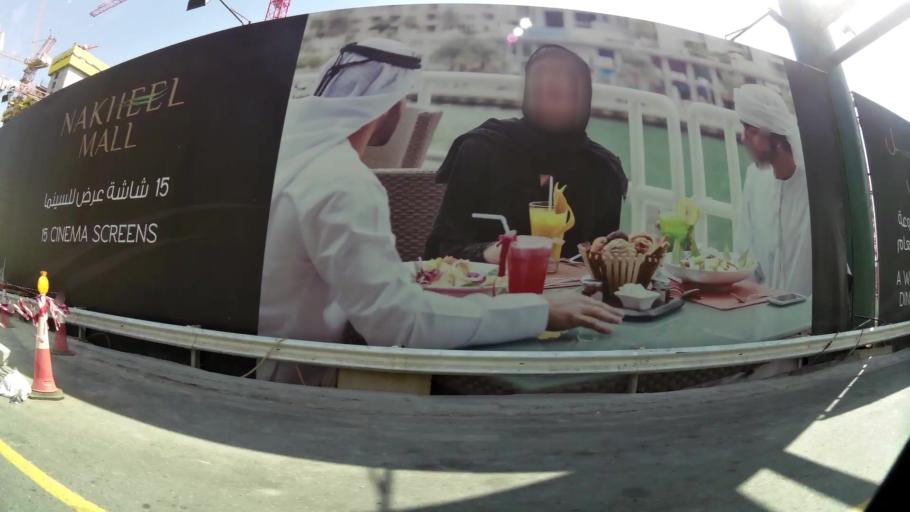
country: AE
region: Dubai
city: Dubai
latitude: 25.1155
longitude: 55.1392
